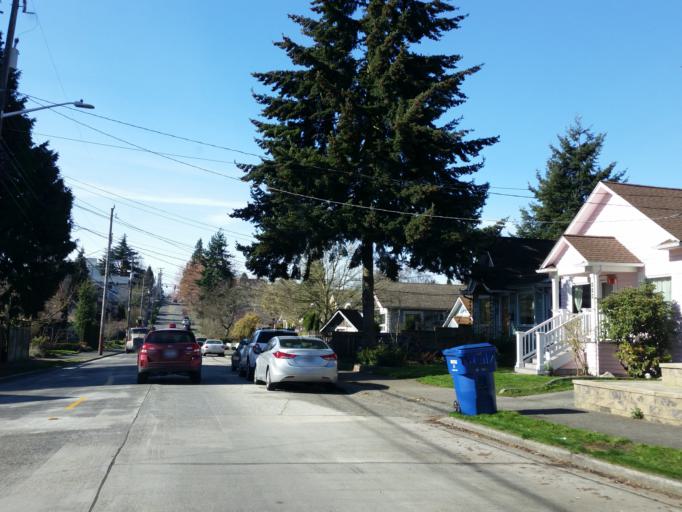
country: US
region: Washington
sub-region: King County
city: Shoreline
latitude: 47.6870
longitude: -122.3507
